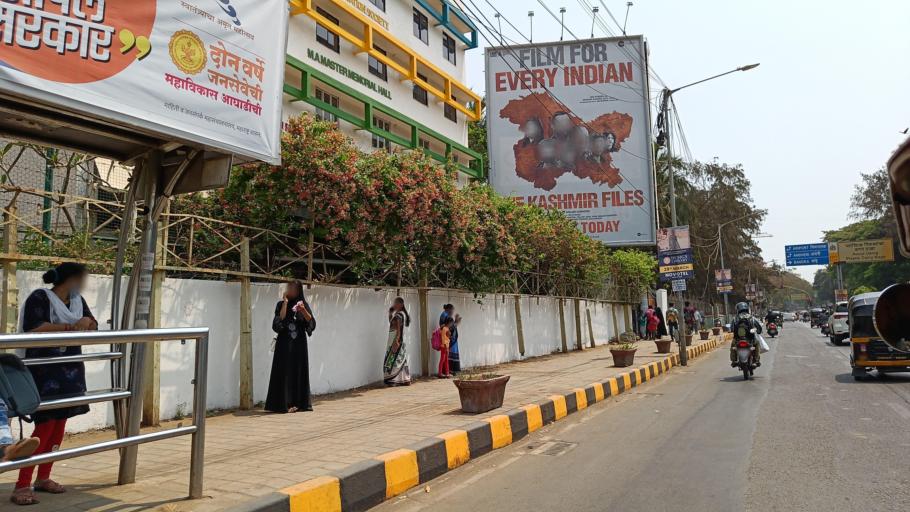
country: IN
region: Maharashtra
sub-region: Mumbai Suburban
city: Mumbai
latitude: 19.0848
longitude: 72.8326
